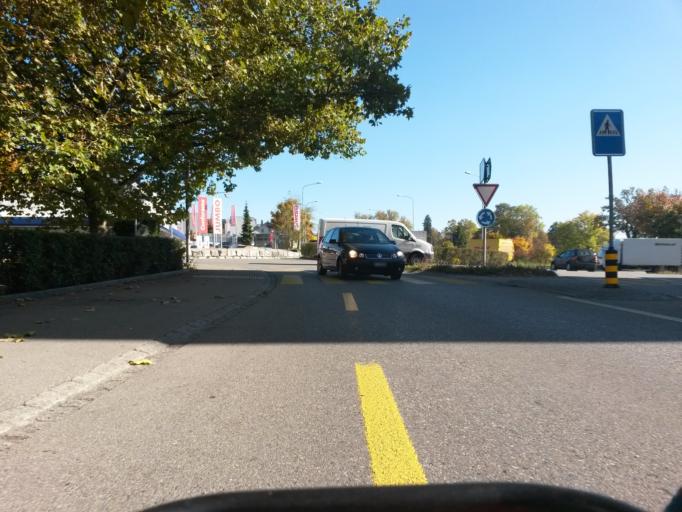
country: CH
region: Solothurn
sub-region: Bezirk Solothurn
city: Solothurn
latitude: 47.2110
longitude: 7.5260
